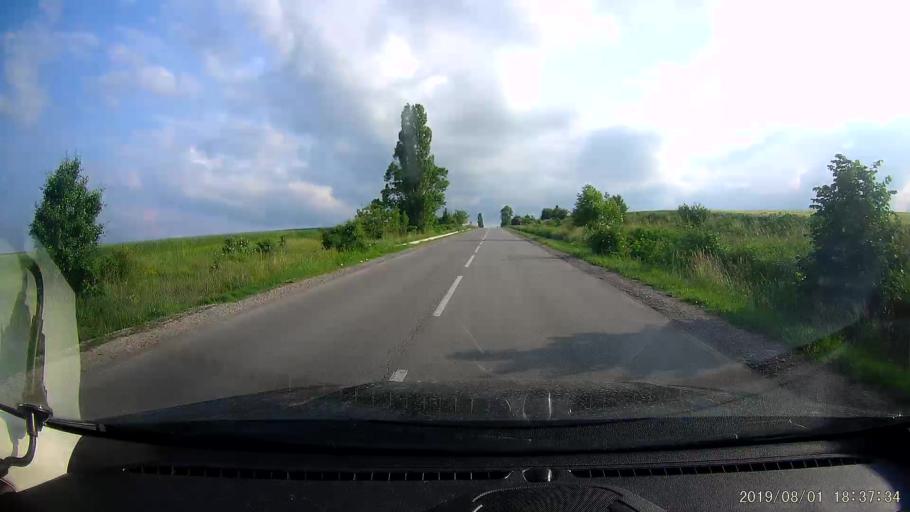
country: BG
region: Shumen
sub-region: Obshtina Khitrino
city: Gara Khitrino
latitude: 43.4184
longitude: 26.9287
